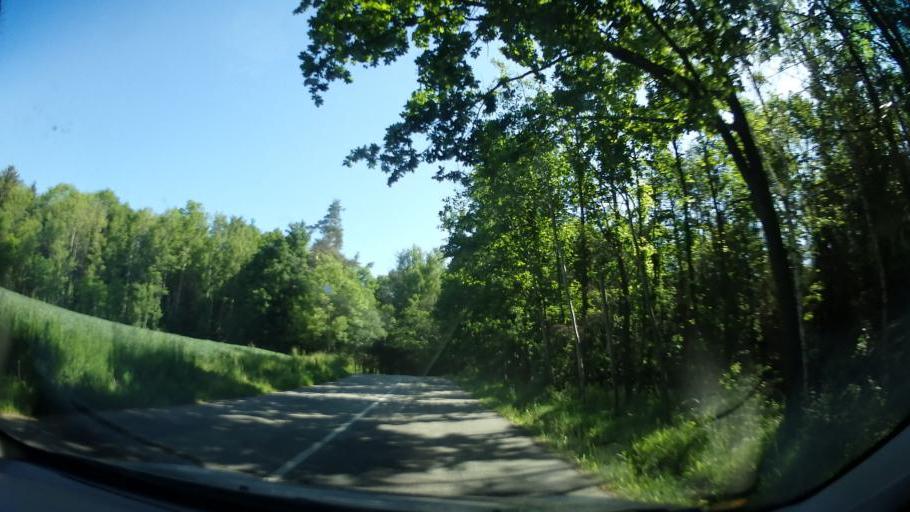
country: CZ
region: South Moravian
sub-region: Okres Blansko
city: Letovice
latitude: 49.5796
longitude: 16.5849
